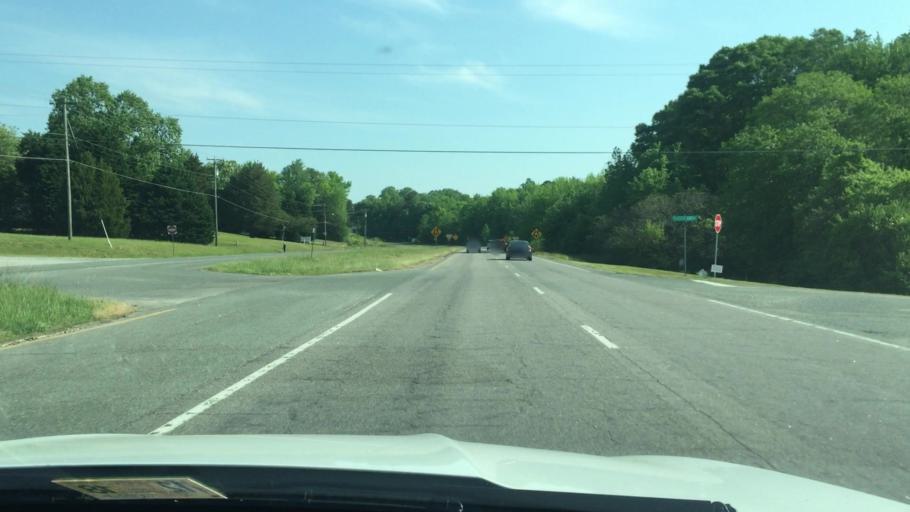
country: US
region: Virginia
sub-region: Lancaster County
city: Kilmarnock
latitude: 37.6946
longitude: -76.3744
